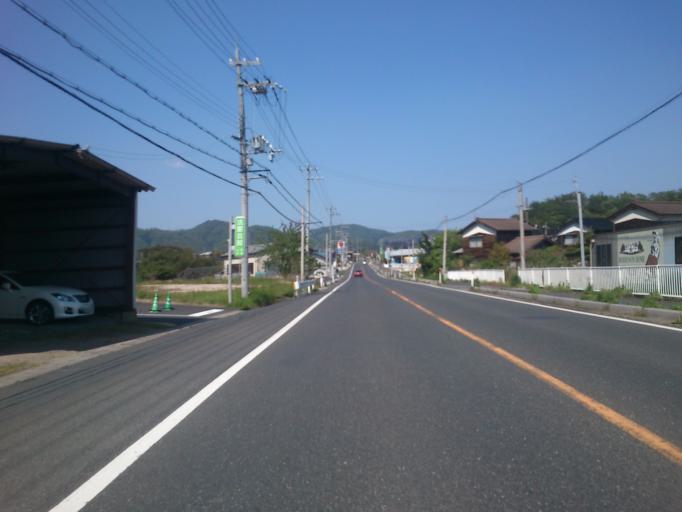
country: JP
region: Kyoto
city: Miyazu
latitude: 35.6823
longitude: 135.0419
